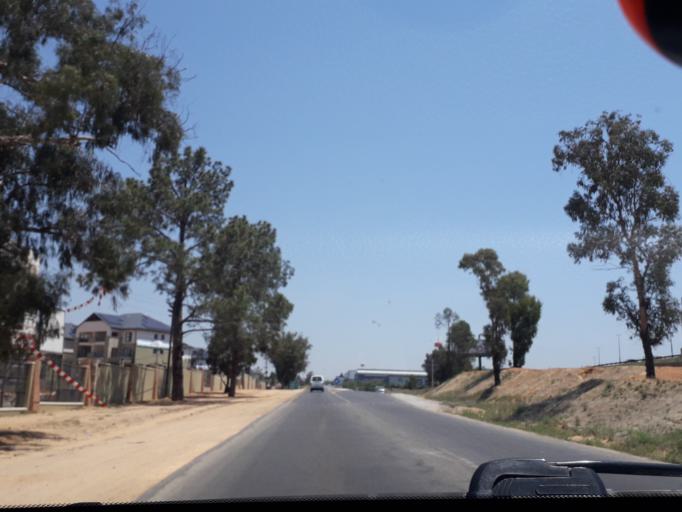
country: ZA
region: Gauteng
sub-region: City of Johannesburg Metropolitan Municipality
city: Midrand
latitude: -26.0390
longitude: 28.1076
